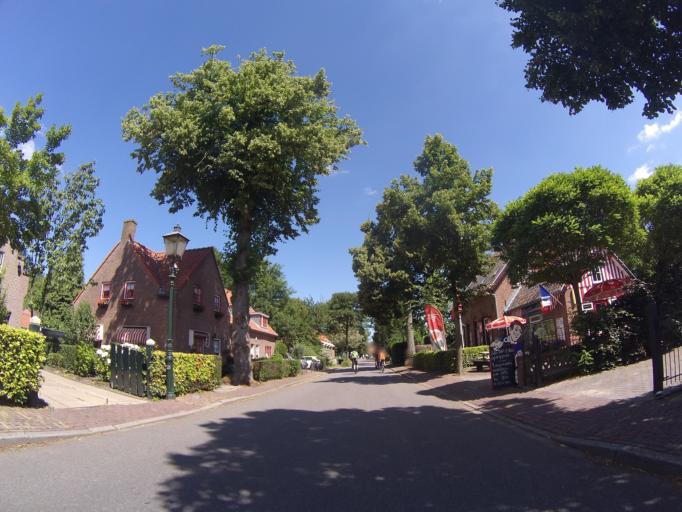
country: NL
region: Utrecht
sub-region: Stichtse Vecht
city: Spechtenkamp
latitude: 52.1213
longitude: 4.9982
